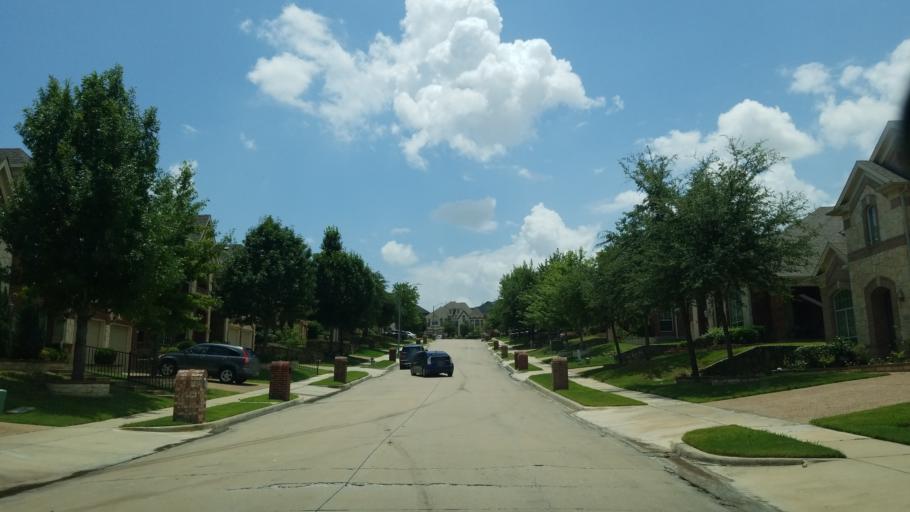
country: US
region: Texas
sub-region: Dallas County
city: Coppell
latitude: 32.9460
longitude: -96.9672
